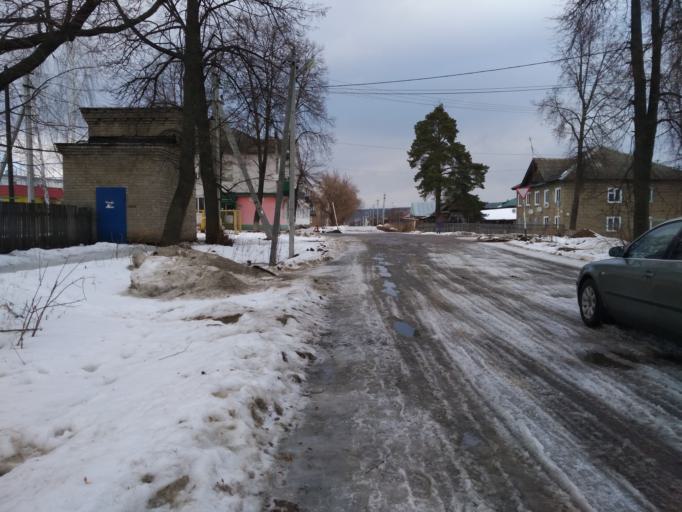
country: RU
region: Kirov
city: Krasnaya Polyana
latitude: 56.2406
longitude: 51.1409
